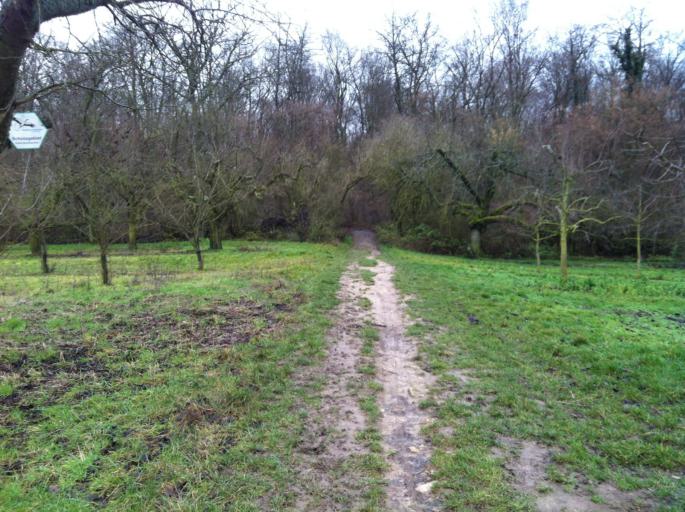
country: DE
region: Rheinland-Pfalz
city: Ober-Olm
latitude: 49.9682
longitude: 8.1712
